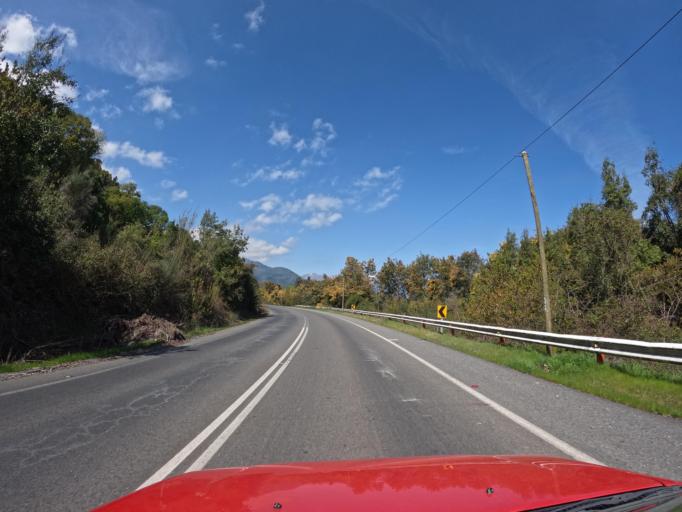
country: CL
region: Maule
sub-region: Provincia de Linares
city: Colbun
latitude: -35.6576
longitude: -71.2477
